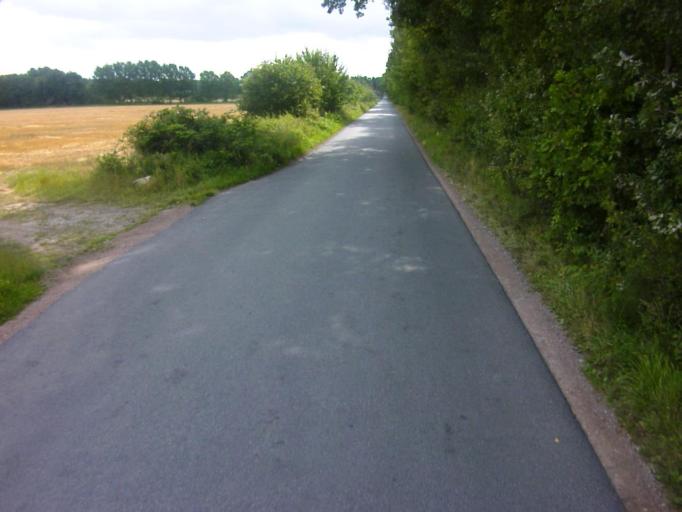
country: SE
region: Blekinge
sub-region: Solvesborgs Kommun
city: Soelvesborg
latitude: 56.0271
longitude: 14.6114
